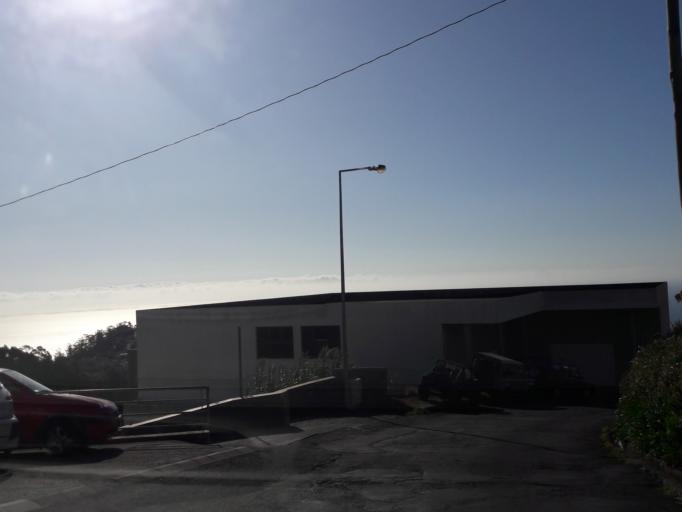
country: PT
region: Madeira
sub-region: Santa Cruz
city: Camacha
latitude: 32.6604
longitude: -16.8613
